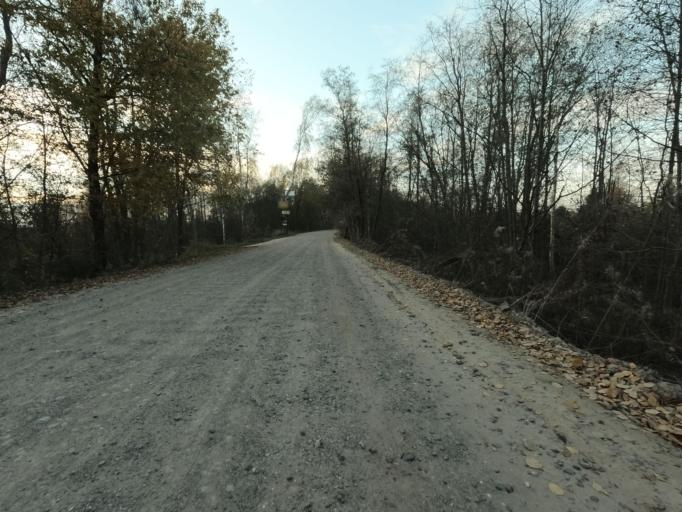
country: RU
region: Leningrad
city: Mga
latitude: 59.7699
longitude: 31.2301
